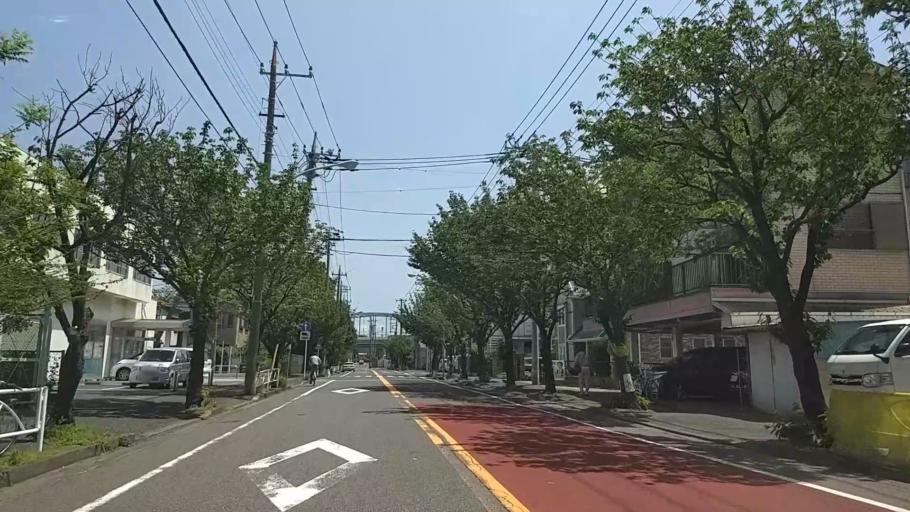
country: JP
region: Kanagawa
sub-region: Kawasaki-shi
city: Kawasaki
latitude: 35.5182
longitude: 139.7211
